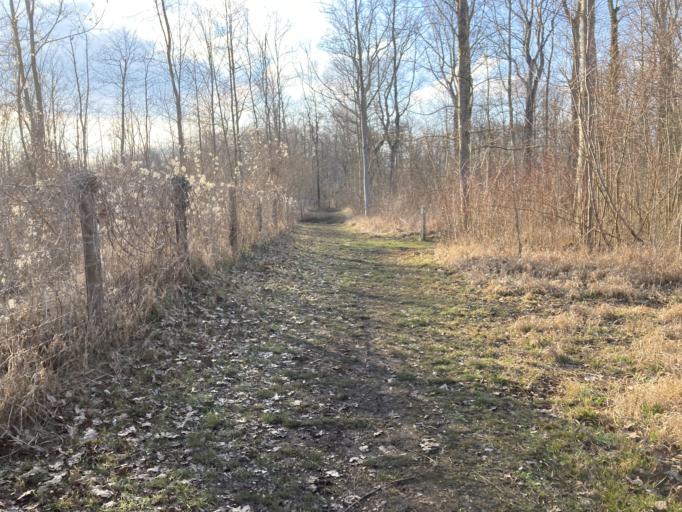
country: FR
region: Nord-Pas-de-Calais
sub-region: Departement du Pas-de-Calais
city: Sailly-Labourse
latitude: 50.5190
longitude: 2.7057
